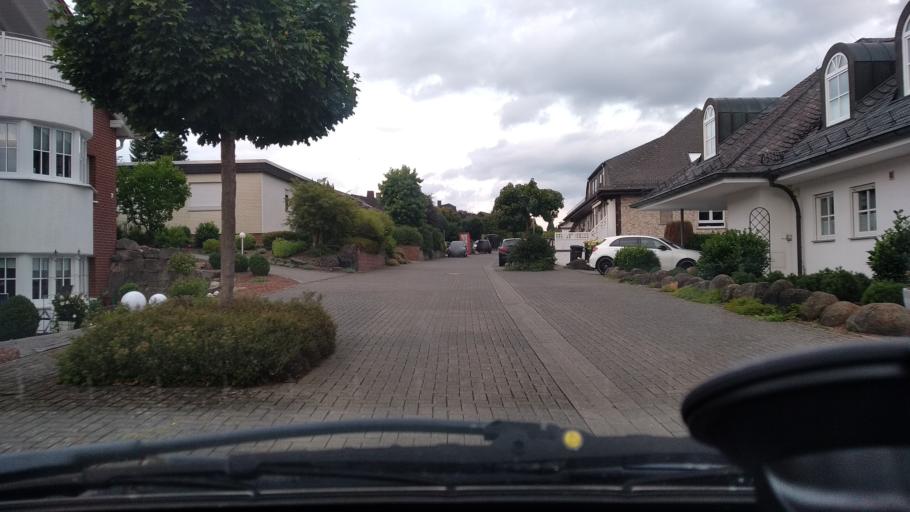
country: DE
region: Hesse
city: Dillenburg
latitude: 50.7749
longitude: 8.2900
